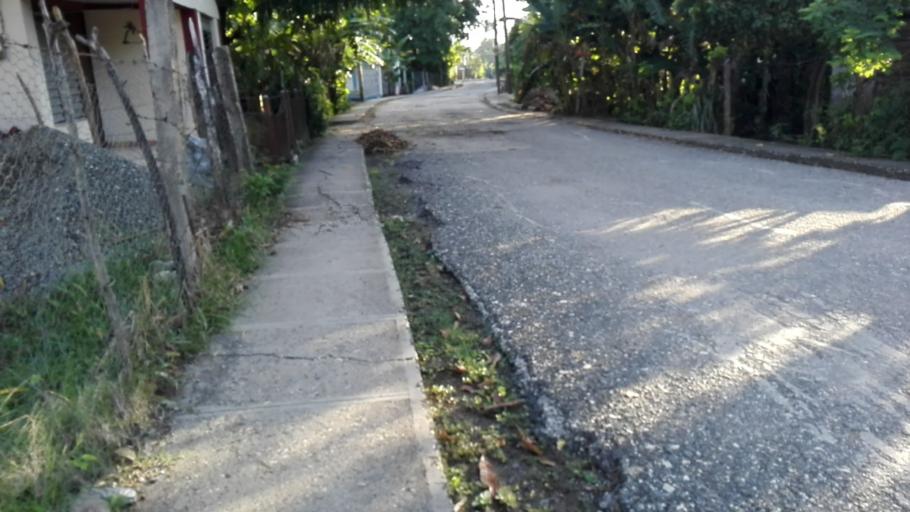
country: CU
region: Granma
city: Bartolome Maso
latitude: 20.1633
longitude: -76.9488
